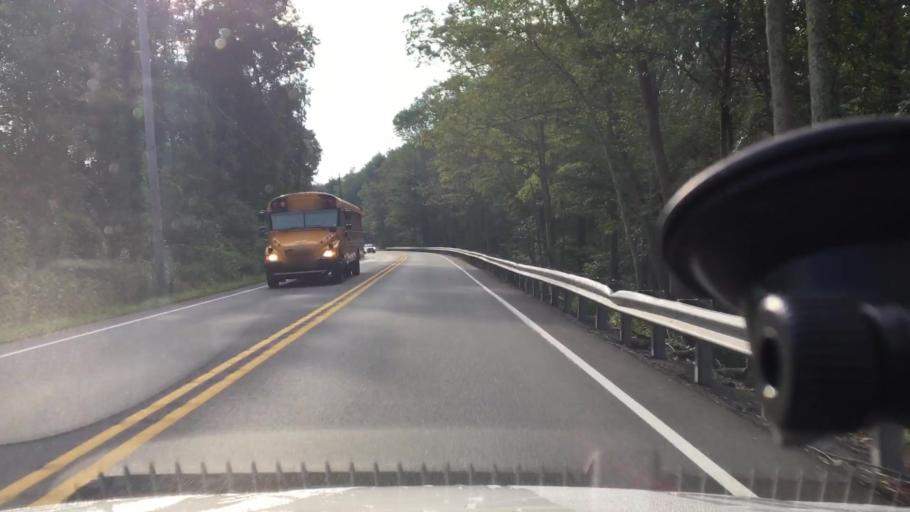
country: US
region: Pennsylvania
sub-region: Monroe County
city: Parkside
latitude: 41.1263
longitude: -75.2947
